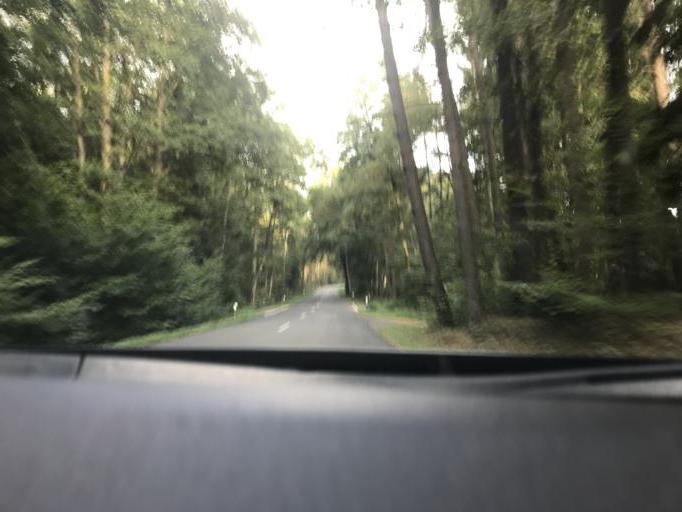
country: DE
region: Lower Saxony
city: Stadensen
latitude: 52.8878
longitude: 10.5215
